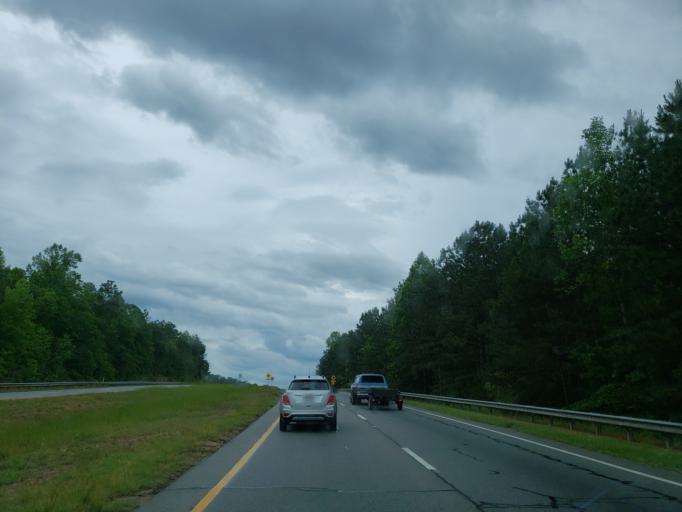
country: US
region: Georgia
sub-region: Haralson County
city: Bremen
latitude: 33.6964
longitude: -85.1561
